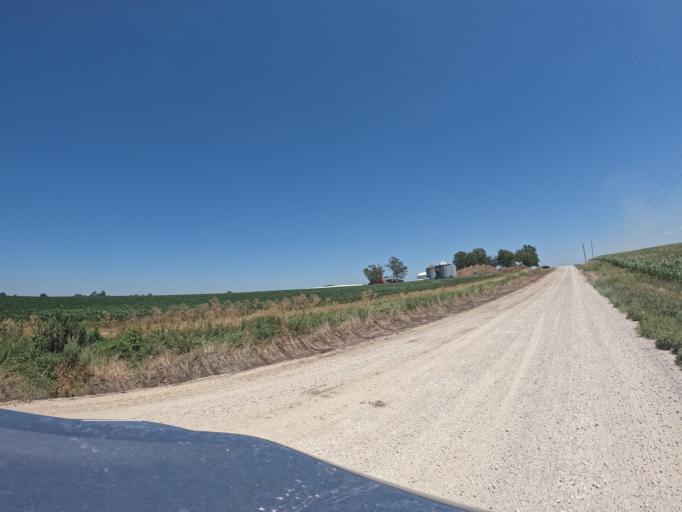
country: US
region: Iowa
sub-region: Keokuk County
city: Sigourney
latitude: 41.4090
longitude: -92.3142
